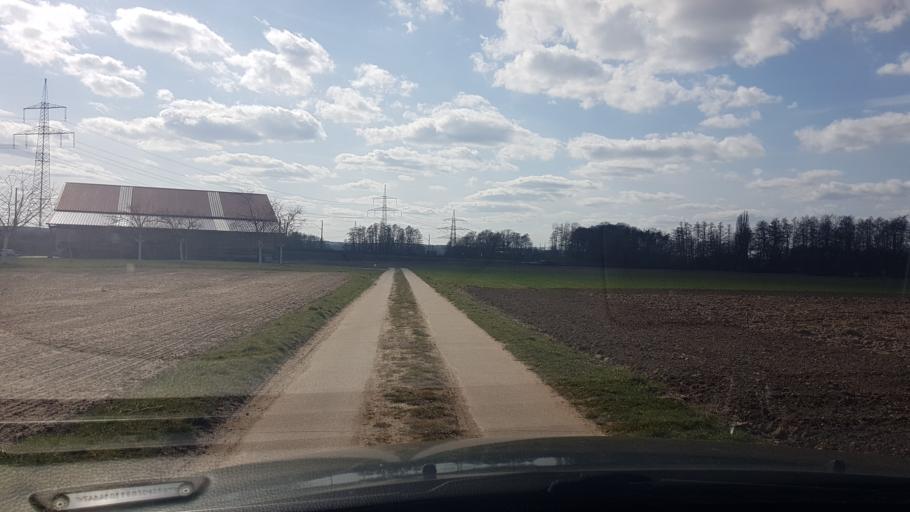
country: DE
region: Bavaria
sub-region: Upper Franconia
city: Bischberg
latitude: 49.9301
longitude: 10.8488
